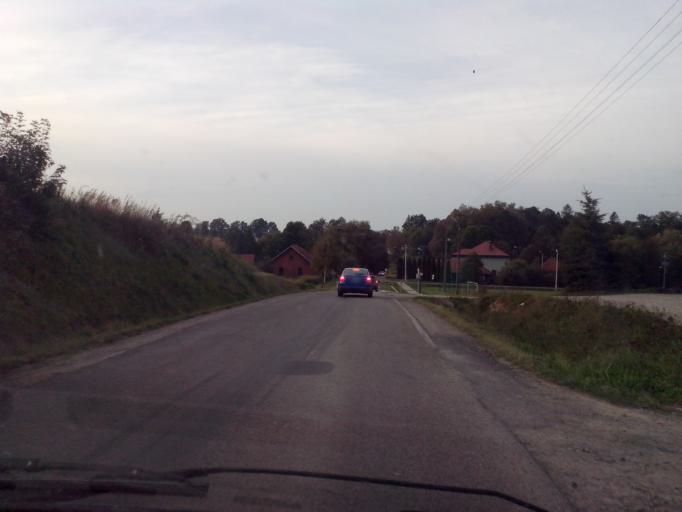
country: PL
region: Subcarpathian Voivodeship
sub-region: Powiat strzyzowski
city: Jawornik
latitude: 49.8144
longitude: 21.8423
